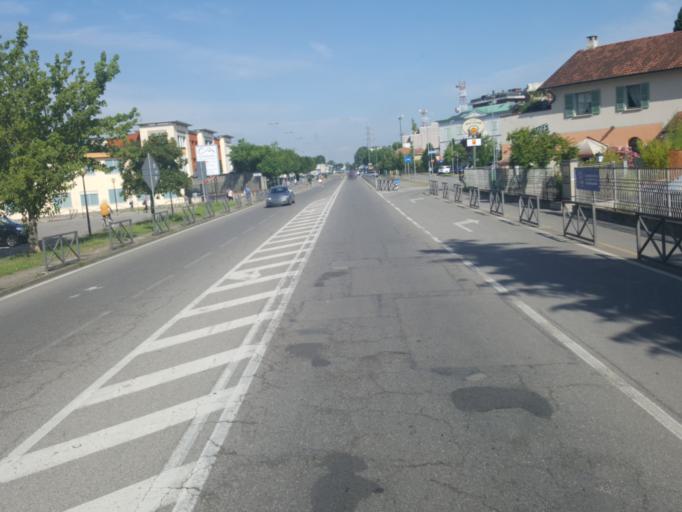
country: IT
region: Lombardy
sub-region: Provincia di Cremona
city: Crema
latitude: 45.3550
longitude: 9.6814
